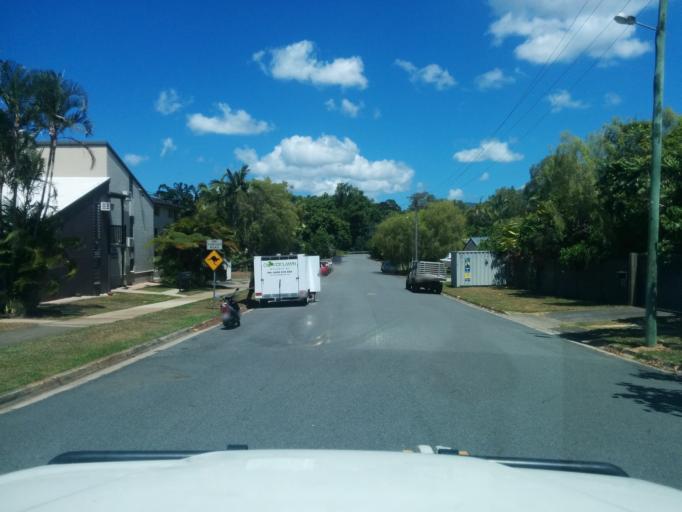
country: AU
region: Queensland
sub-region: Cairns
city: Cairns
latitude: -16.9015
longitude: 145.7443
